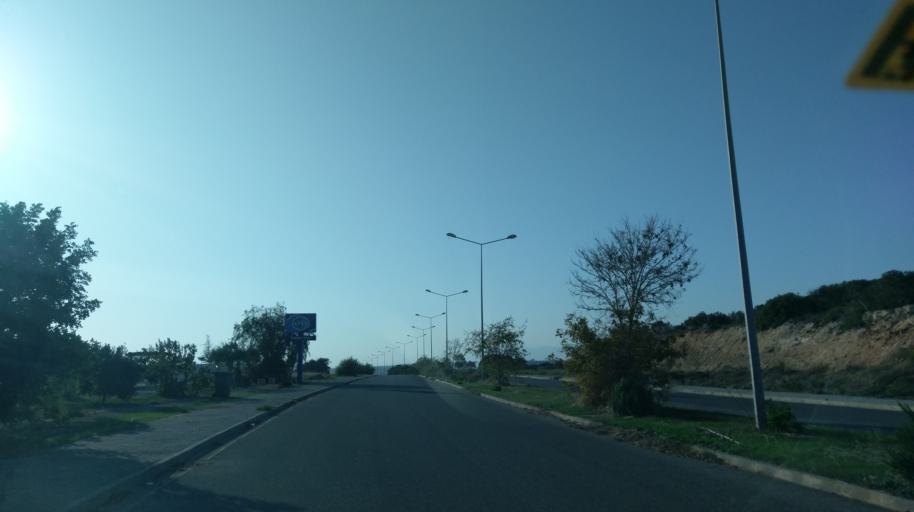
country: CY
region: Ammochostos
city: Leonarisso
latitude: 35.3718
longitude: 34.0836
